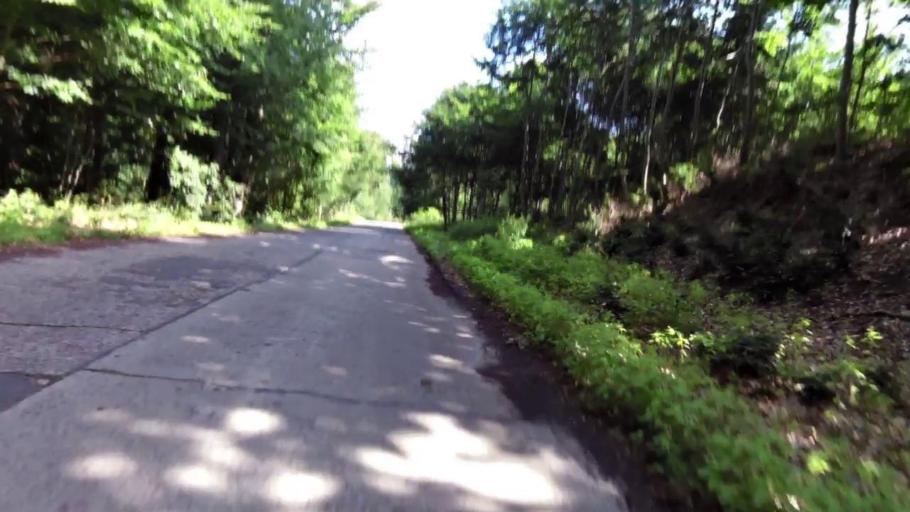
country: PL
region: West Pomeranian Voivodeship
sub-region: Powiat stargardzki
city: Insko
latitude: 53.3926
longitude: 15.5031
